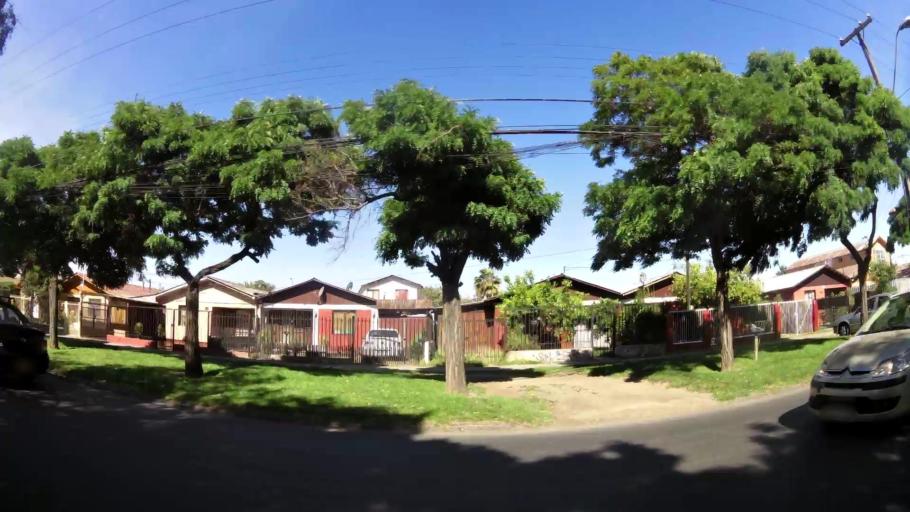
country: CL
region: Santiago Metropolitan
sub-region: Provincia de Santiago
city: Lo Prado
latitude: -33.5206
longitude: -70.7753
